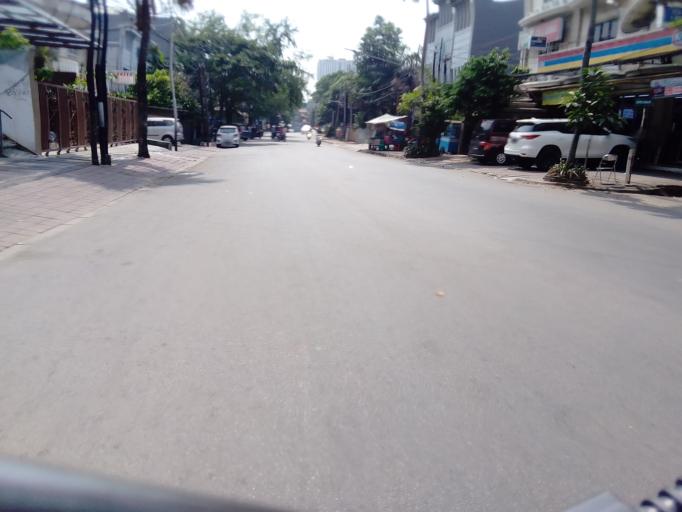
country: ID
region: Jakarta Raya
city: Jakarta
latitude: -6.2074
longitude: 106.8107
